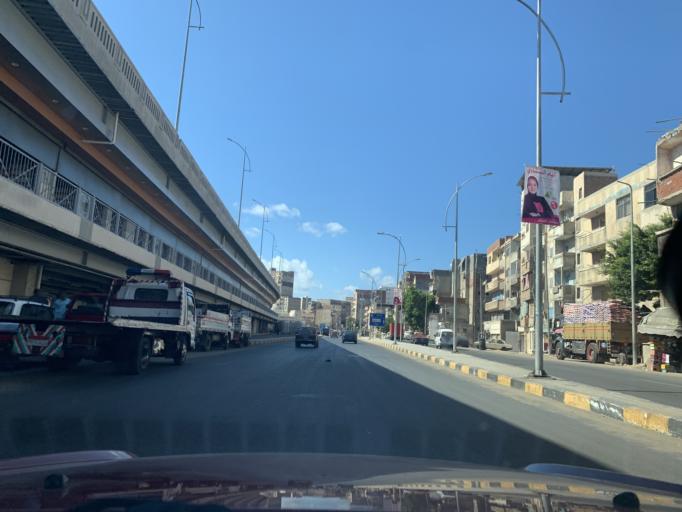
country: EG
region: Alexandria
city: Alexandria
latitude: 31.2244
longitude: 29.9823
